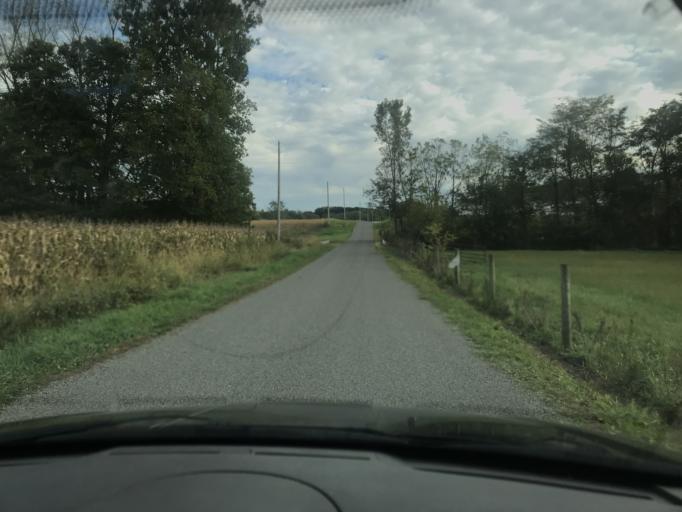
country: US
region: Ohio
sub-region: Logan County
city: West Liberty
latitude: 40.2537
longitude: -83.6965
